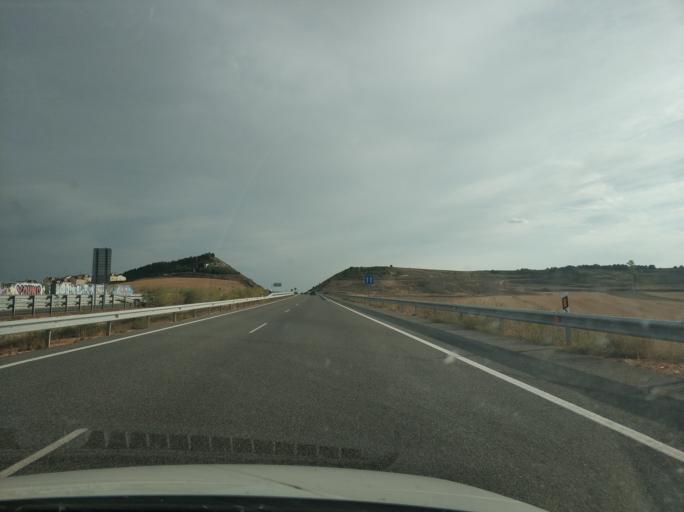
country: ES
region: Castille and Leon
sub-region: Provincia de Burgos
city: Quintanaortuno
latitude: 42.4554
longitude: -3.6896
